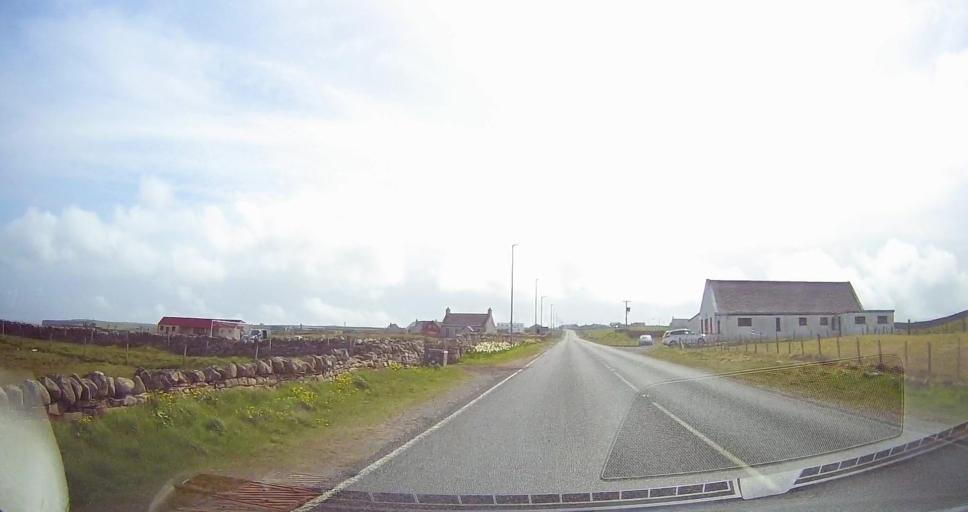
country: GB
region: Scotland
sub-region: Shetland Islands
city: Sandwick
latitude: 59.9262
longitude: -1.2971
